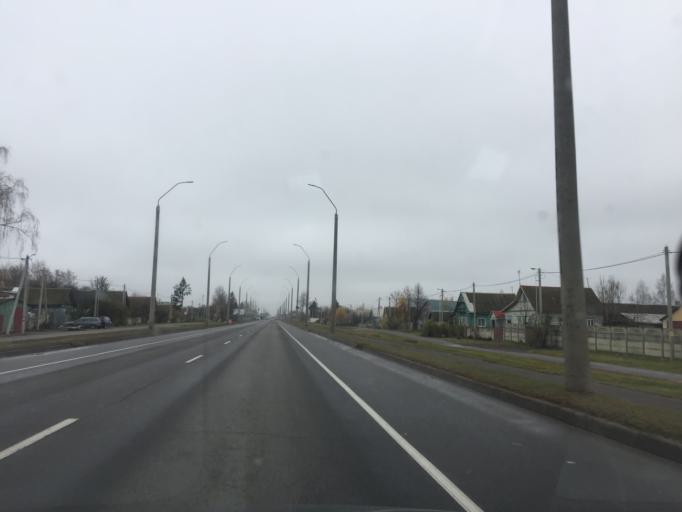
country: BY
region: Mogilev
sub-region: Mahilyowski Rayon
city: Veyno
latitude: 53.8505
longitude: 30.3592
